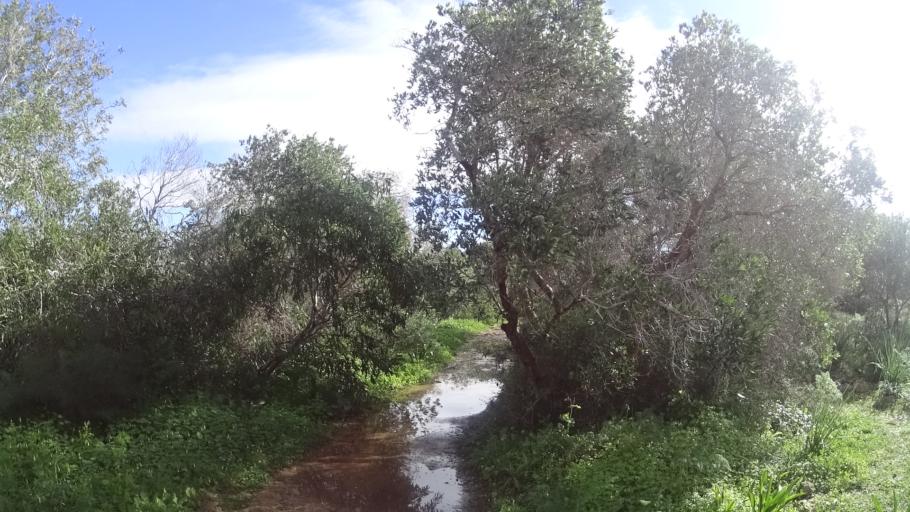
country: MT
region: Il-Mellieha
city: Mellieha
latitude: 35.9490
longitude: 14.3789
